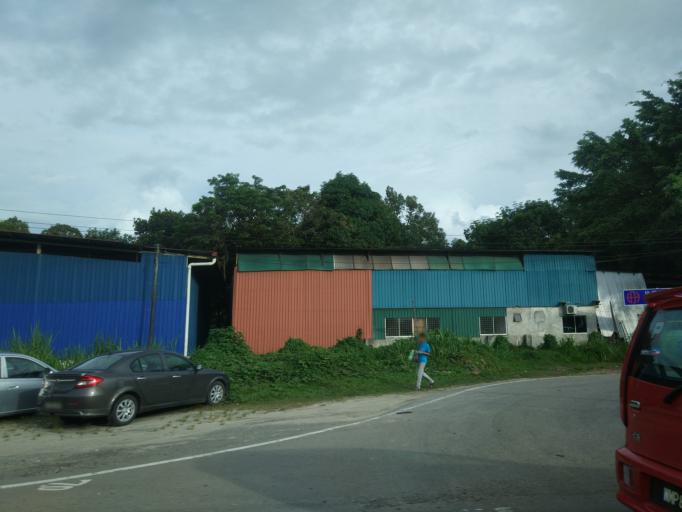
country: MY
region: Sabah
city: Kota Kinabalu
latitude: 6.0409
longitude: 116.1527
